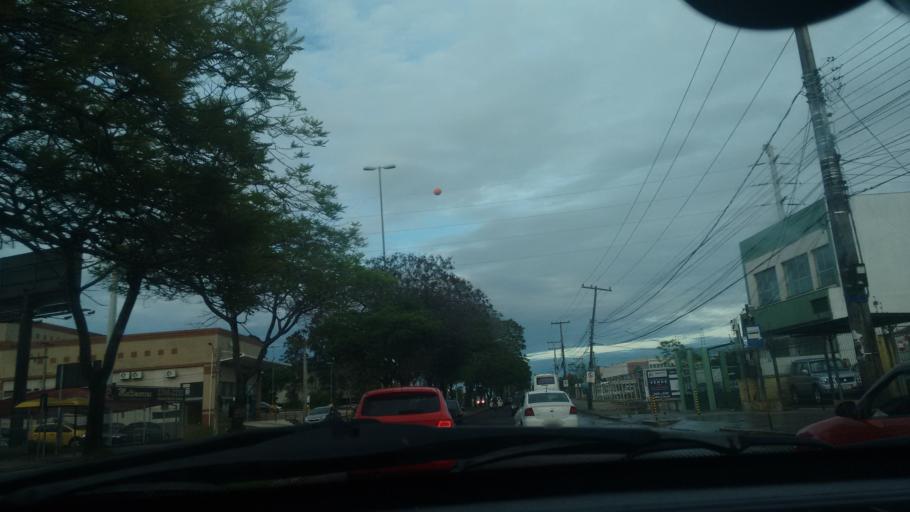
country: BR
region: Rio Grande do Sul
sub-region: Cachoeirinha
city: Cachoeirinha
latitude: -29.9978
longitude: -51.1379
